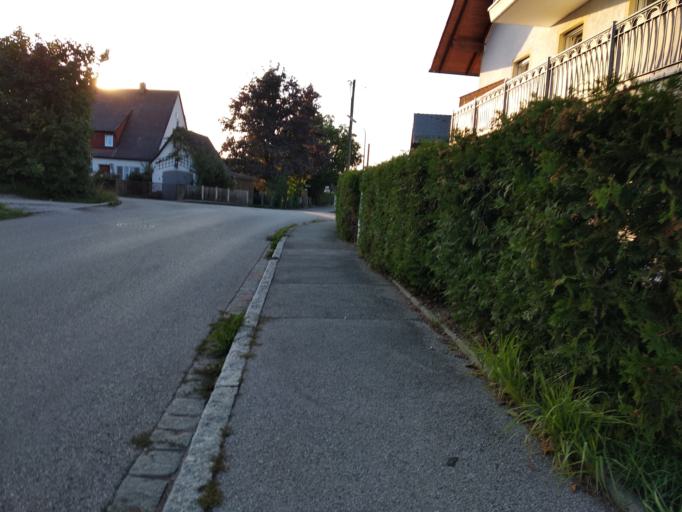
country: DE
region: Bavaria
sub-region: Upper Bavaria
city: Steinhoring
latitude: 48.0882
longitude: 12.0331
